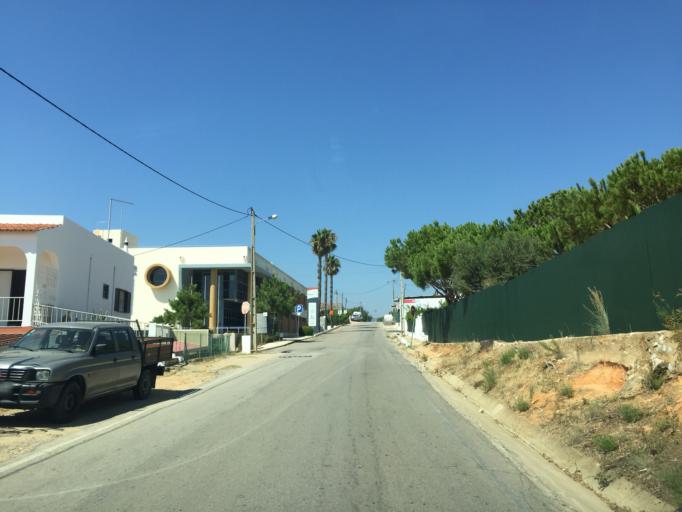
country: PT
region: Faro
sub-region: Faro
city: Faro
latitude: 37.0398
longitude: -7.8963
